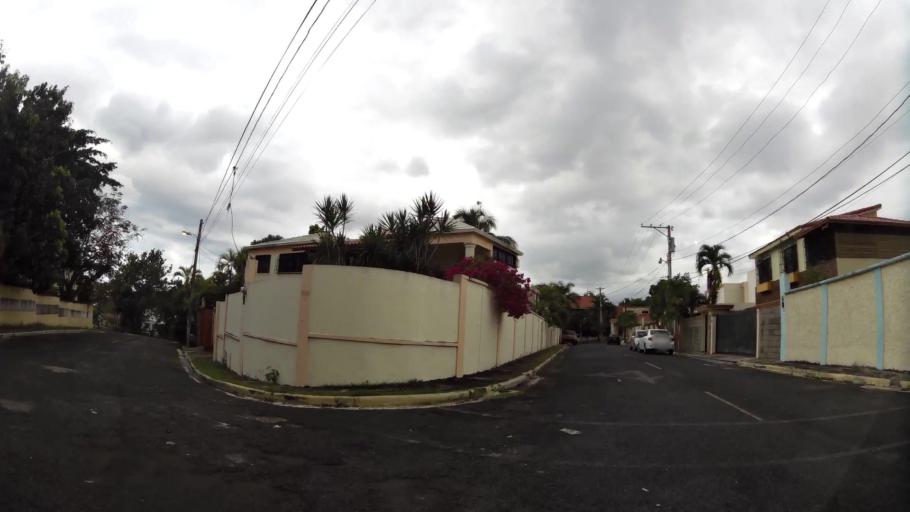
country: DO
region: Nacional
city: La Agustina
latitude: 18.5060
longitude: -69.9342
